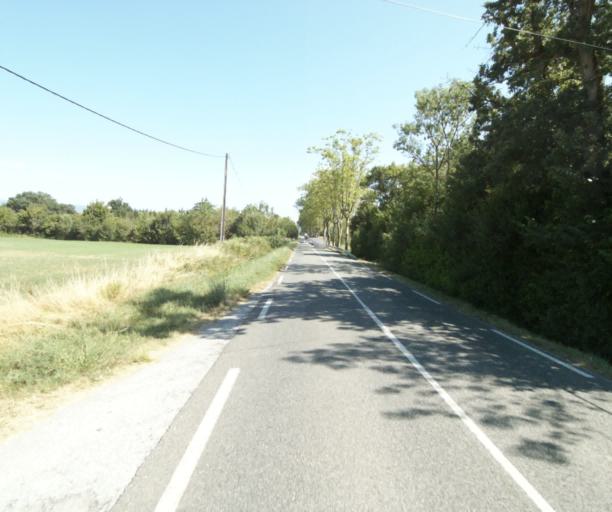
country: FR
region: Midi-Pyrenees
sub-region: Departement de la Haute-Garonne
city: Saint-Felix-Lauragais
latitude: 43.4916
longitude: 1.9025
